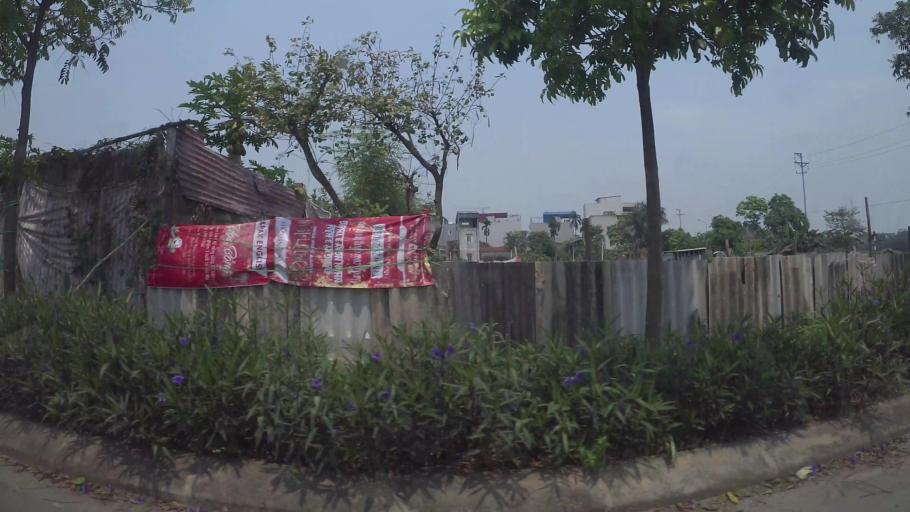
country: VN
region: Ha Noi
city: Van Dien
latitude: 20.9483
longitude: 105.8397
